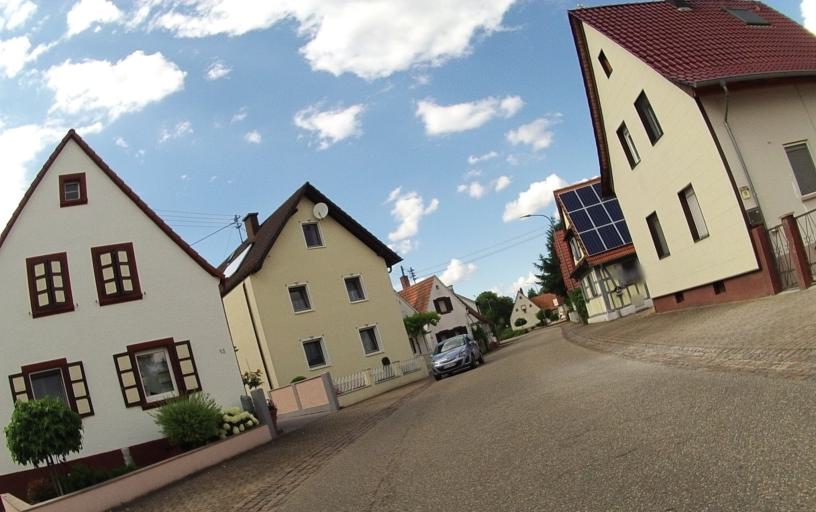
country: DE
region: Rheinland-Pfalz
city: Scheibenhardt
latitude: 48.9821
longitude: 8.1365
